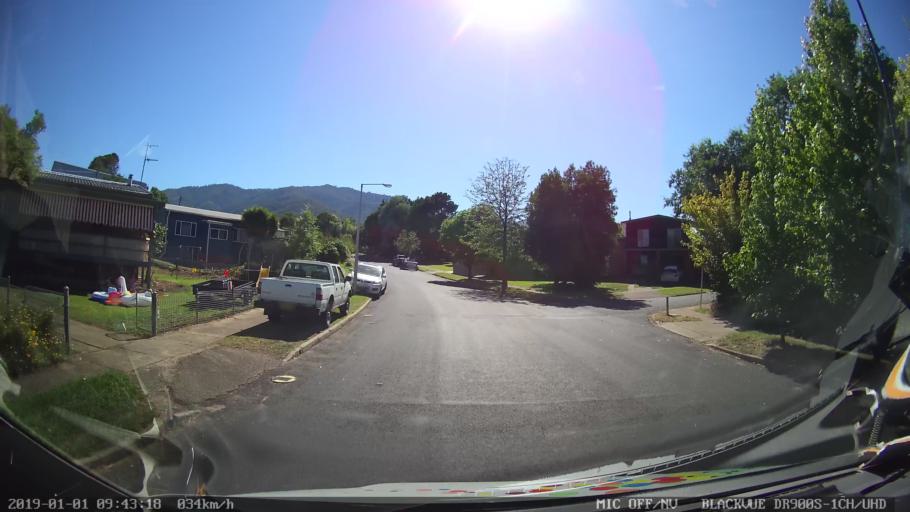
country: AU
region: New South Wales
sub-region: Snowy River
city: Jindabyne
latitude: -36.2153
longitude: 148.1335
